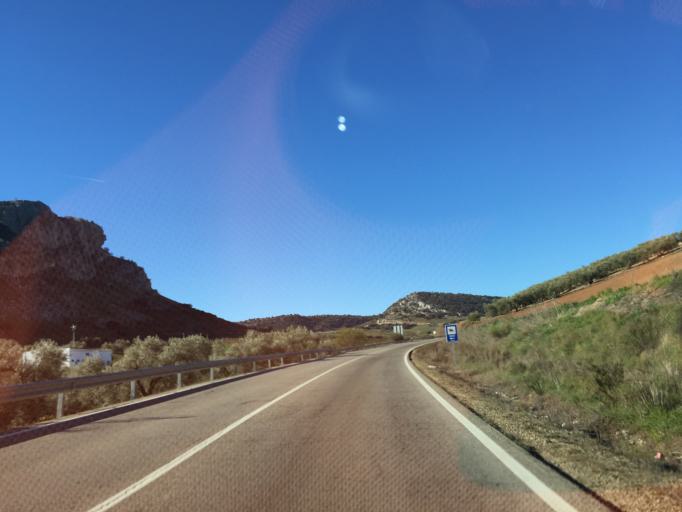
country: ES
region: Andalusia
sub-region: Provincia de Malaga
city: Cuevas del Becerro
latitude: 36.8658
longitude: -5.0518
